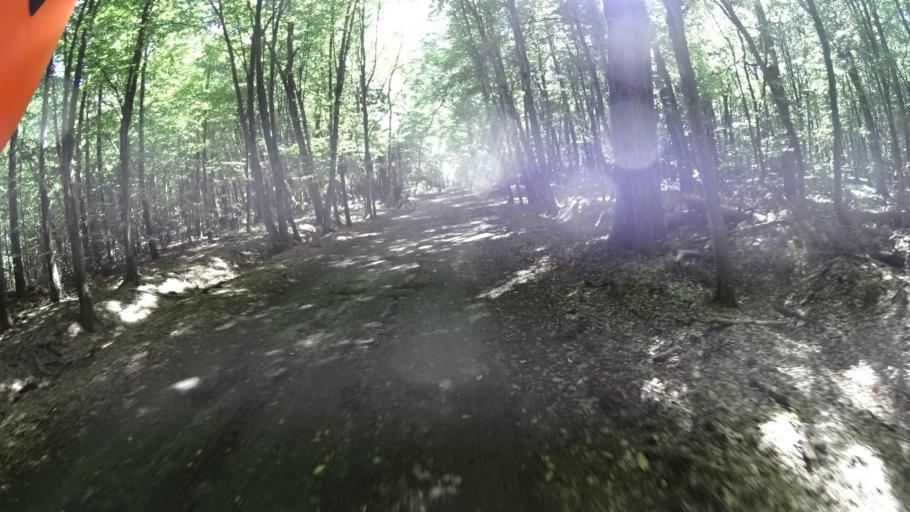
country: PL
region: Masovian Voivodeship
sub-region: Powiat piaseczynski
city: Jozefoslaw
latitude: 52.1211
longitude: 21.0551
